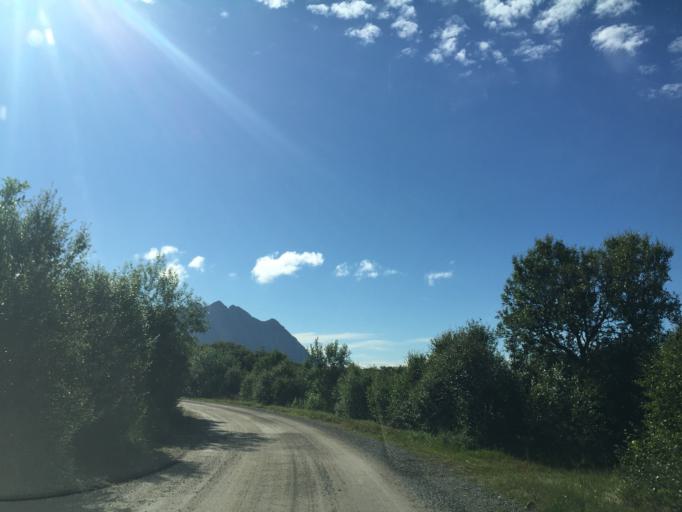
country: NO
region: Nordland
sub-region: Vagan
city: Kabelvag
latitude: 68.3601
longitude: 14.4489
